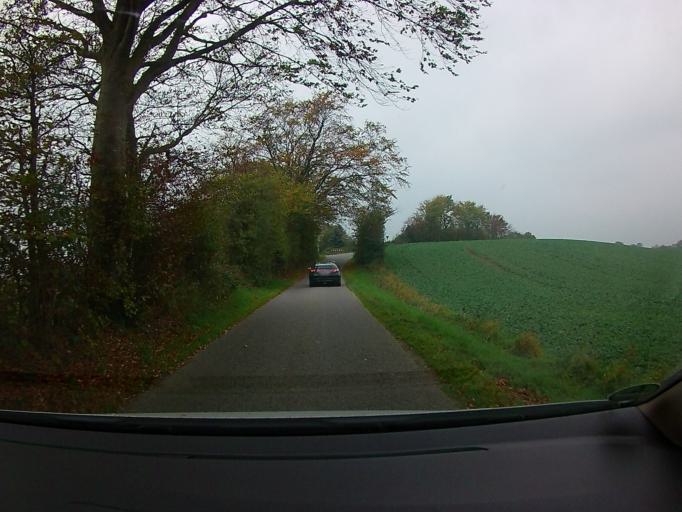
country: DE
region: Schleswig-Holstein
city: Wees
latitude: 54.8623
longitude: 9.4804
